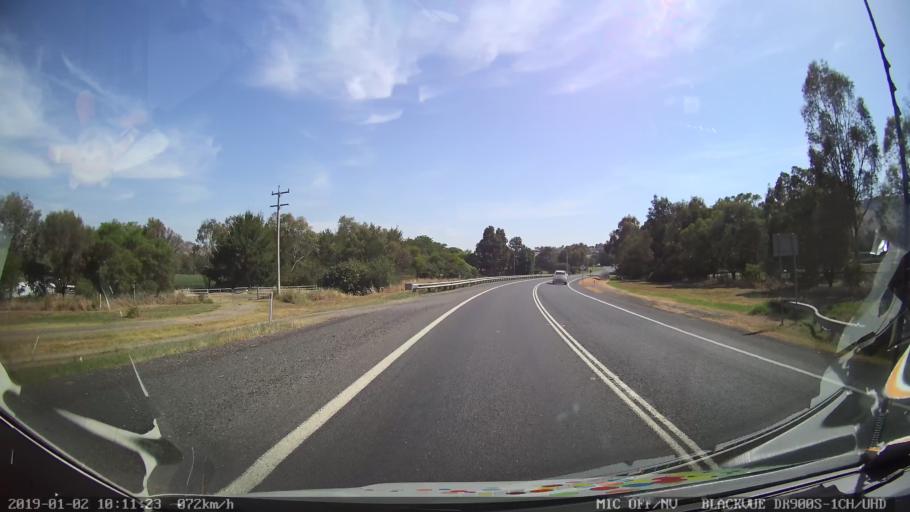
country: AU
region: New South Wales
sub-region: Gundagai
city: Gundagai
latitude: -35.0933
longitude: 148.0919
